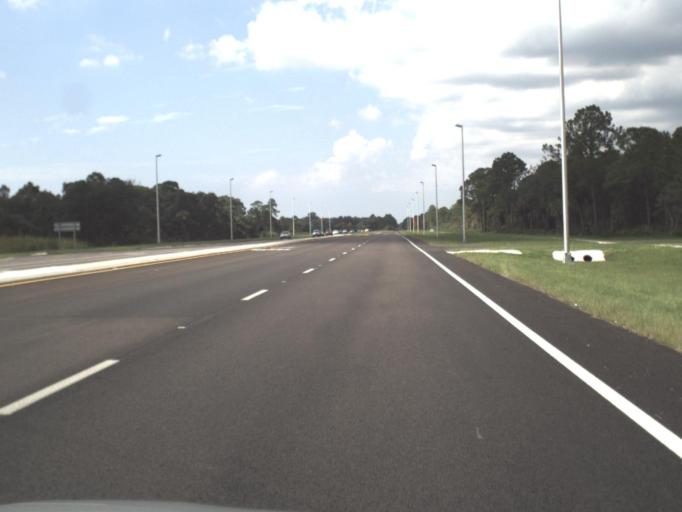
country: US
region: Florida
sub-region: Sarasota County
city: Warm Mineral Springs
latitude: 27.0436
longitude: -82.3016
